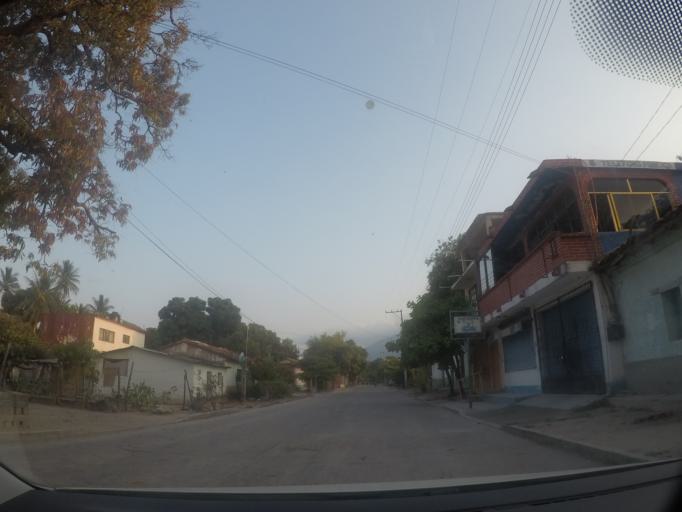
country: MX
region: Oaxaca
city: San Jeronimo Ixtepec
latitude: 16.5846
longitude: -95.2077
